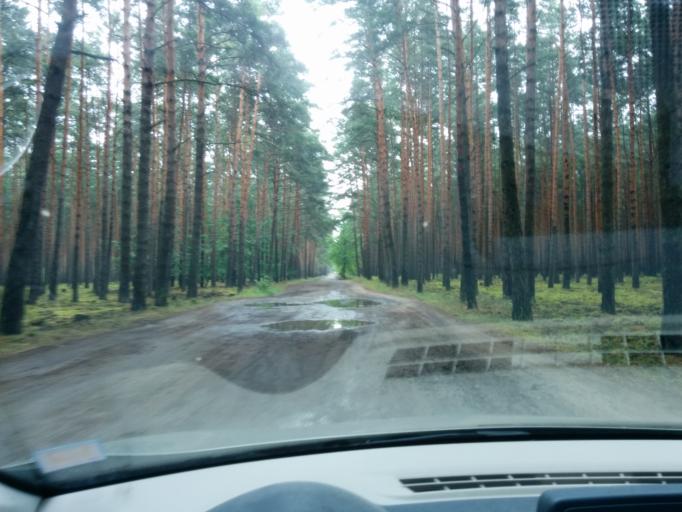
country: DE
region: Brandenburg
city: Gross Koris
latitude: 52.2257
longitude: 13.7543
